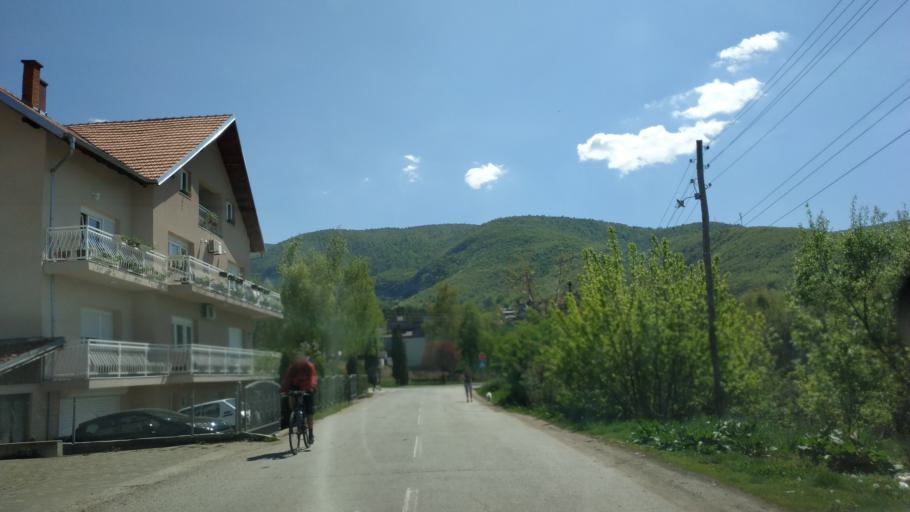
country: RS
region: Central Serbia
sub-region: Zajecarski Okrug
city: Soko Banja
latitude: 43.6462
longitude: 21.8820
